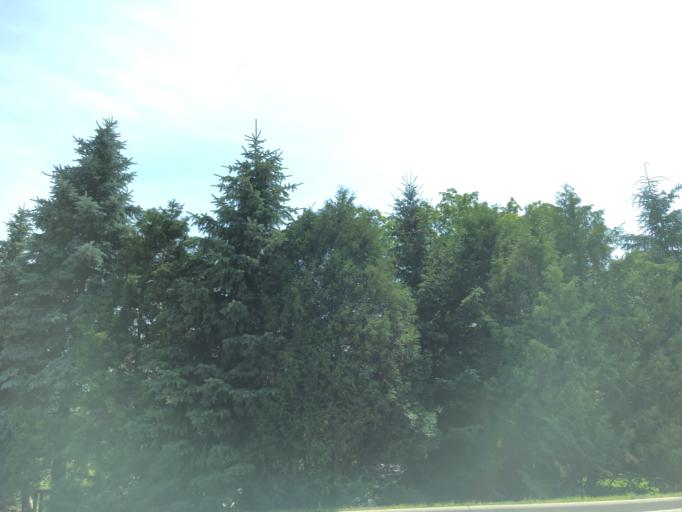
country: US
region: Minnesota
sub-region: Douglas County
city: Alexandria
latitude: 45.9310
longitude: -95.3773
